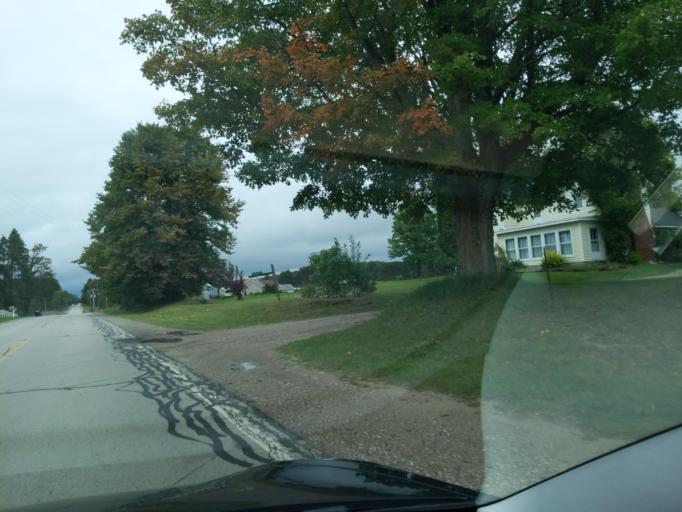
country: US
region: Michigan
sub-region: Grand Traverse County
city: Kingsley
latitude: 44.5887
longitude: -85.3529
